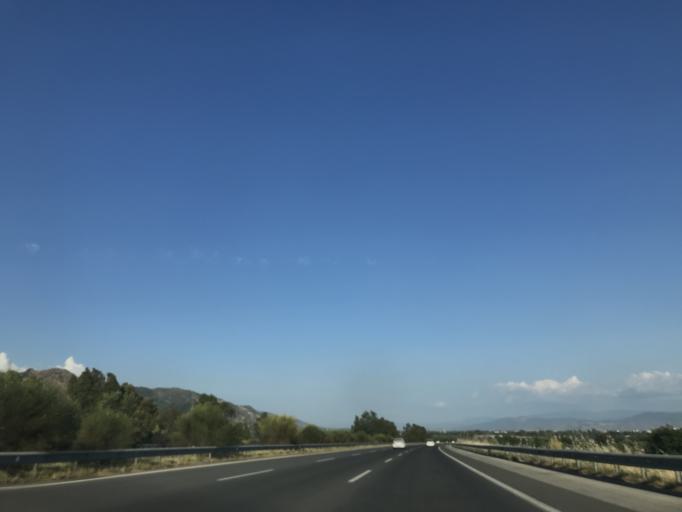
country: TR
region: Aydin
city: Incirliova
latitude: 37.8754
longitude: 27.6959
